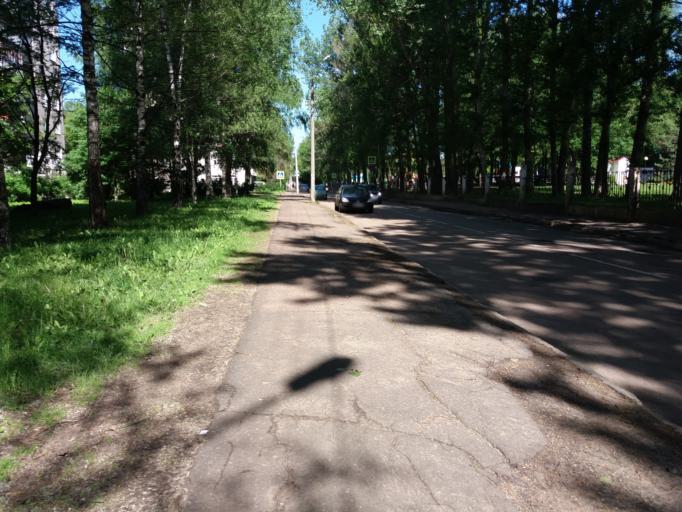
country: RU
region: Jaroslavl
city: Yaroslavl
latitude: 57.6350
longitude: 39.8555
